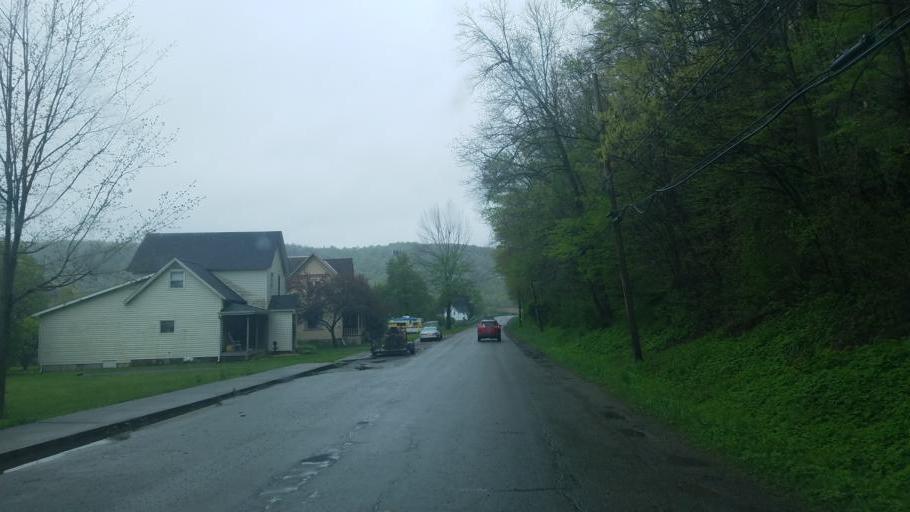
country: US
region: Pennsylvania
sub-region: Potter County
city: Coudersport
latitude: 41.7728
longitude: -78.0236
